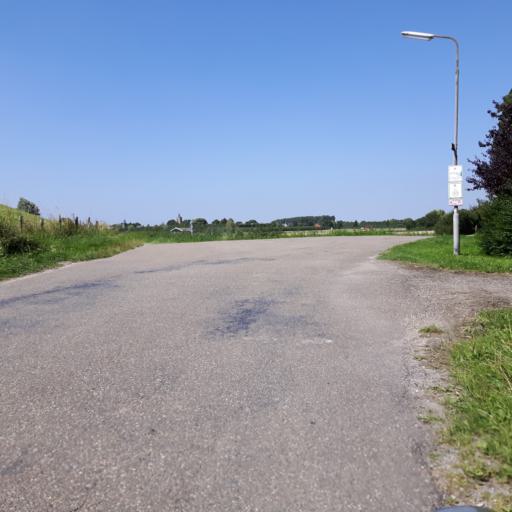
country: NL
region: Zeeland
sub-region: Gemeente Reimerswaal
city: Yerseke
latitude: 51.4114
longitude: 4.0747
